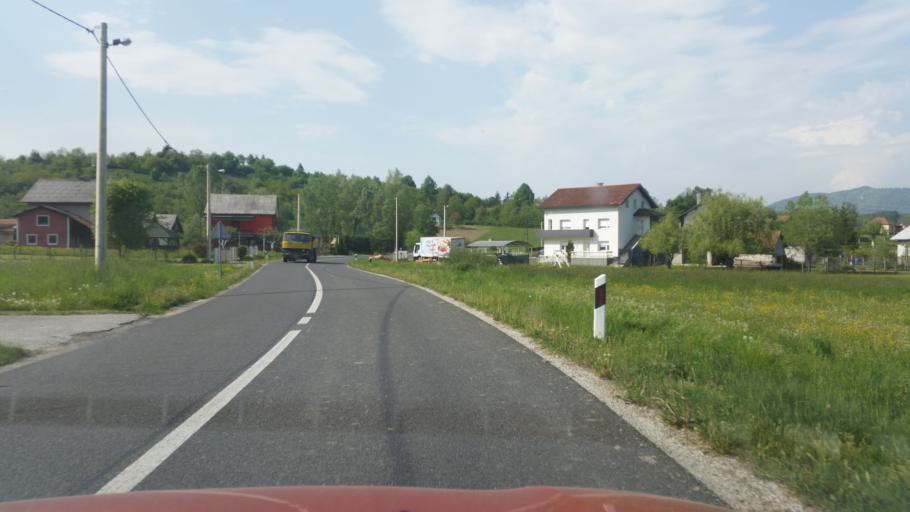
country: HR
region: Krapinsko-Zagorska
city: Radoboj
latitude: 46.2173
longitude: 15.9653
